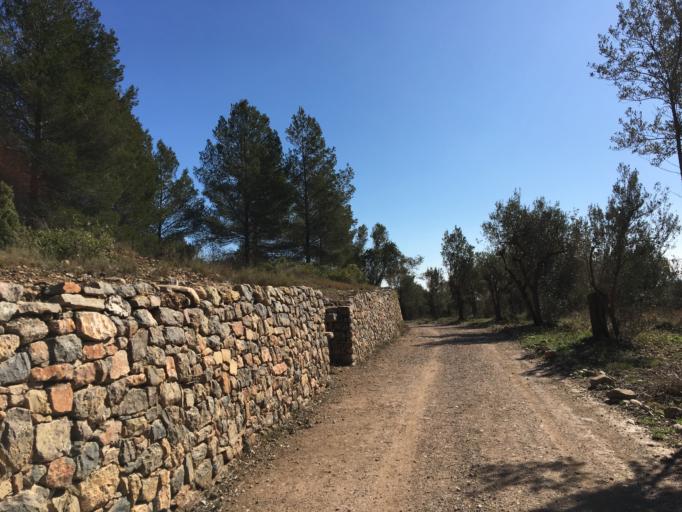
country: ES
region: Catalonia
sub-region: Provincia de Barcelona
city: Collbato
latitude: 41.5750
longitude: 1.8171
